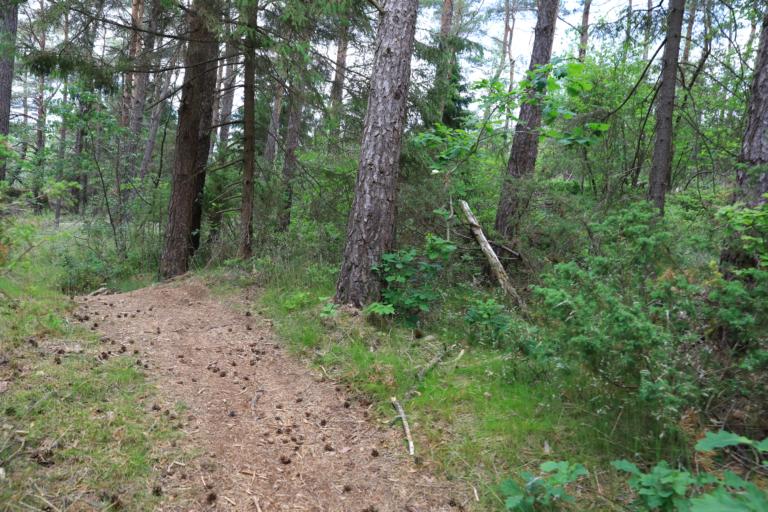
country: SE
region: Halland
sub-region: Varbergs Kommun
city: Varberg
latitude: 57.1670
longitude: 12.2508
